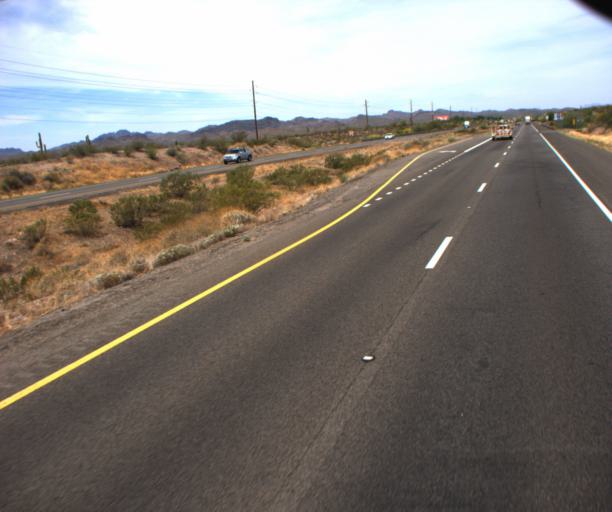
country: US
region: Arizona
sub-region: Maricopa County
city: Wickenburg
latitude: 33.8594
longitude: -112.6278
